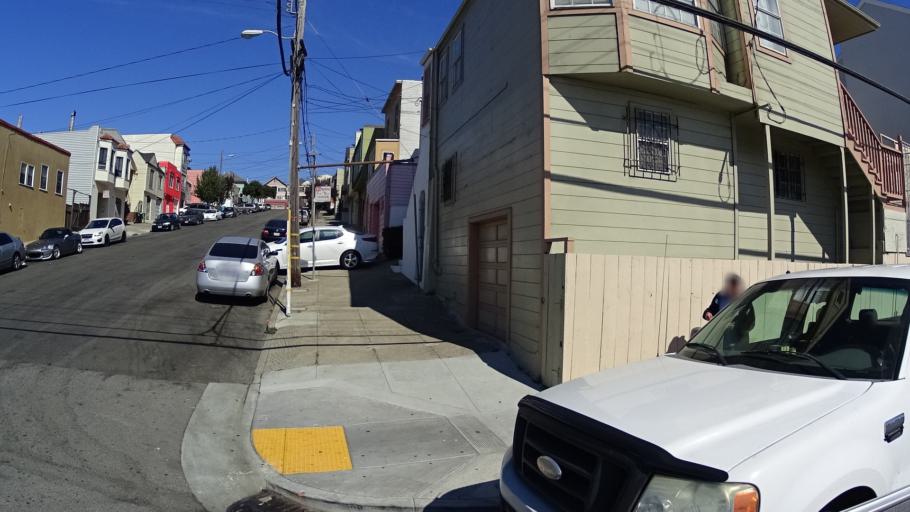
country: US
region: California
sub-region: San Mateo County
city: Brisbane
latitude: 37.7295
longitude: -122.3934
